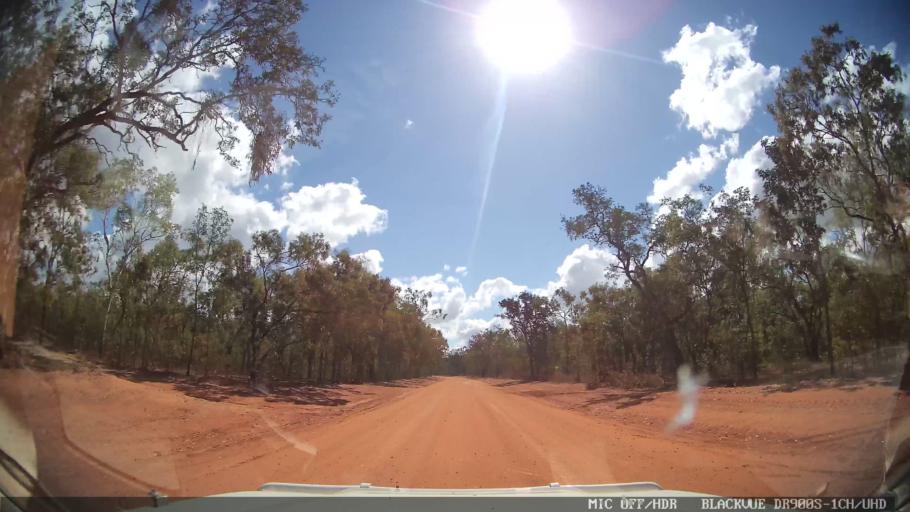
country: AU
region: Queensland
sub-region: Cook
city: Cooktown
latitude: -15.1926
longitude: 144.3747
